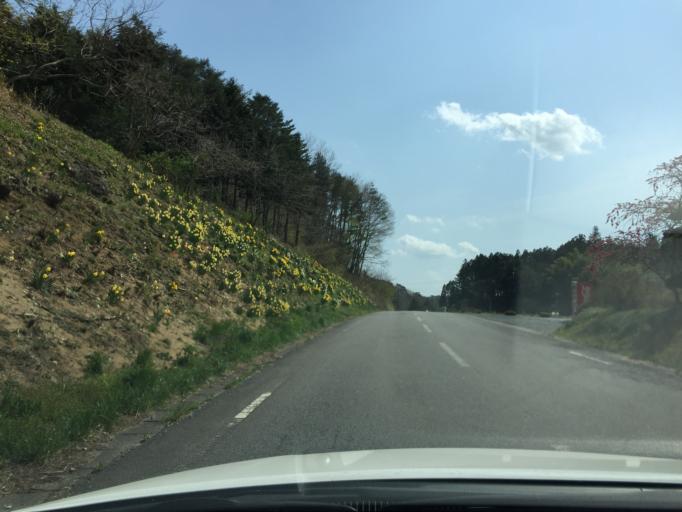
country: JP
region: Fukushima
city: Namie
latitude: 37.3992
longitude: 140.8018
